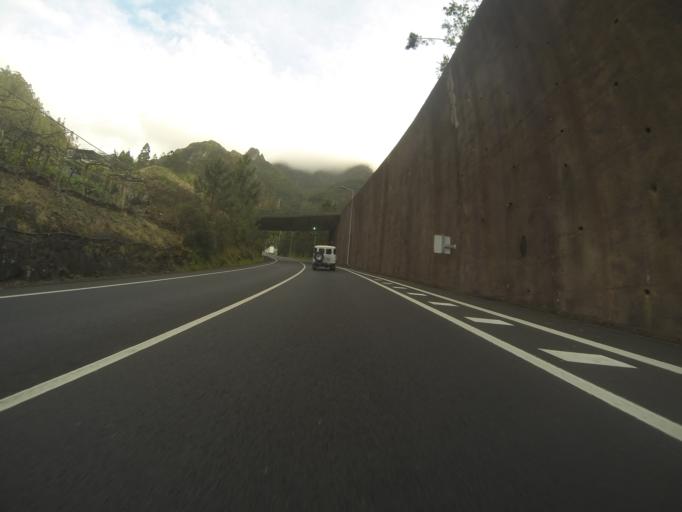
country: PT
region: Madeira
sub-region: Sao Vicente
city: Sao Vicente
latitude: 32.7688
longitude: -17.0307
